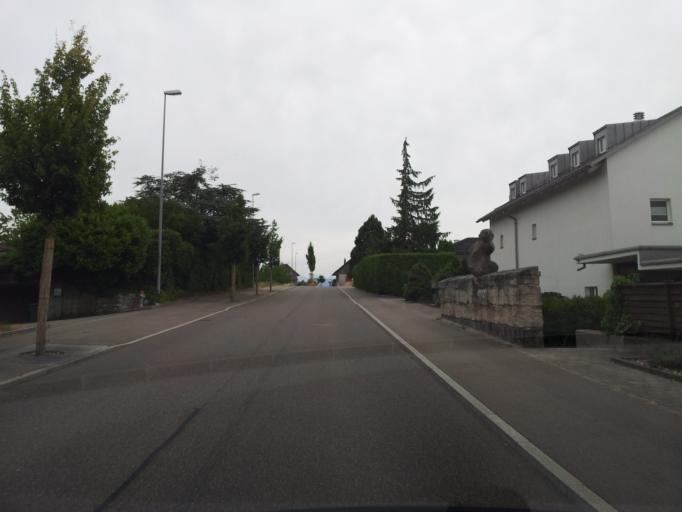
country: CH
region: Aargau
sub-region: Bezirk Bremgarten
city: Berikon
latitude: 47.3461
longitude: 8.3782
